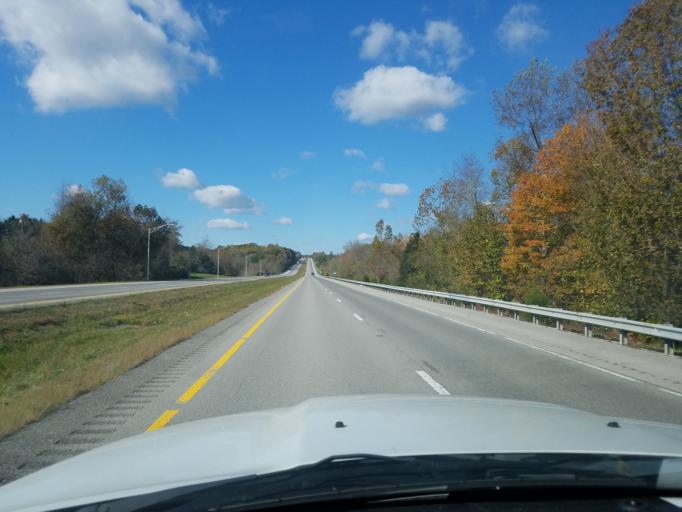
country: US
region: Kentucky
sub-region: Metcalfe County
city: Edmonton
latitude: 36.9964
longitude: -85.6607
